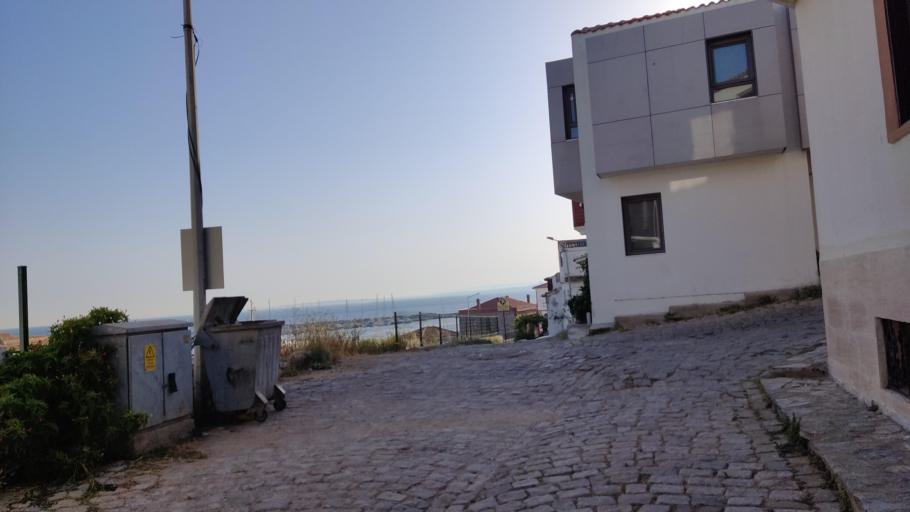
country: TR
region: Canakkale
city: Bozcaada
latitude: 39.8328
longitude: 26.0721
